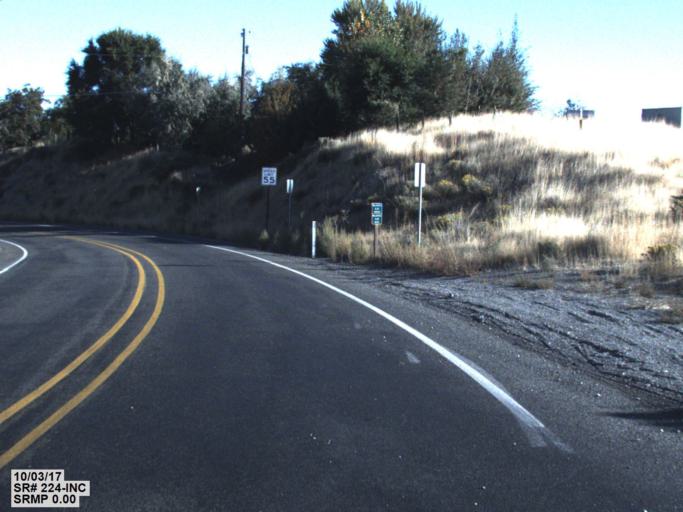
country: US
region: Washington
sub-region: Benton County
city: Benton City
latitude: 46.2526
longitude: -119.4719
